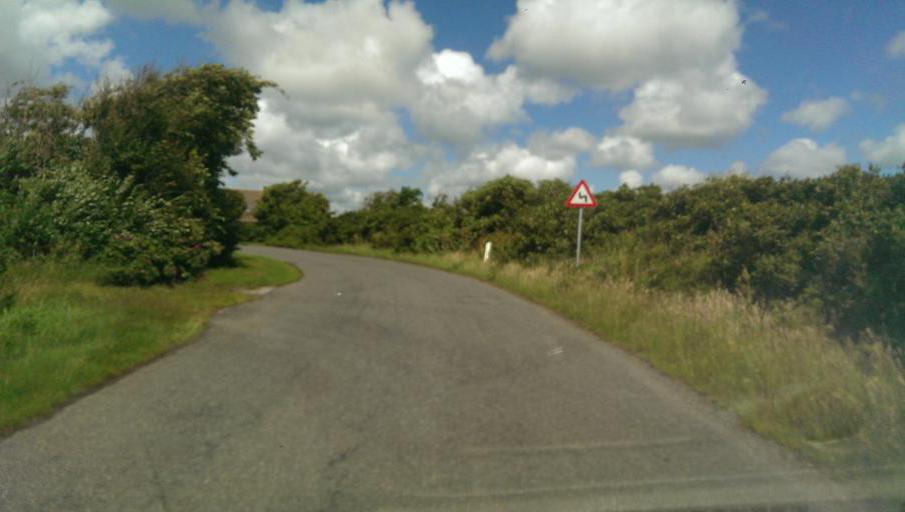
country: DK
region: Central Jutland
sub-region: Holstebro Kommune
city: Ulfborg
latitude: 56.2495
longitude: 8.2334
